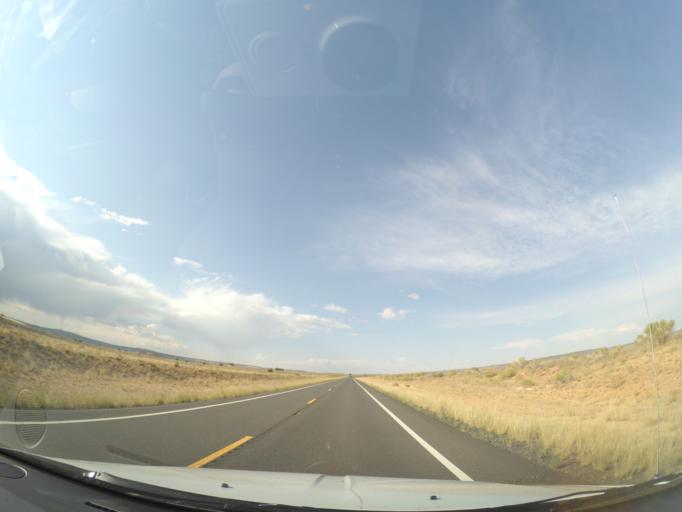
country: US
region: Arizona
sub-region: Coconino County
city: Tuba City
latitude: 36.4527
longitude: -111.4242
